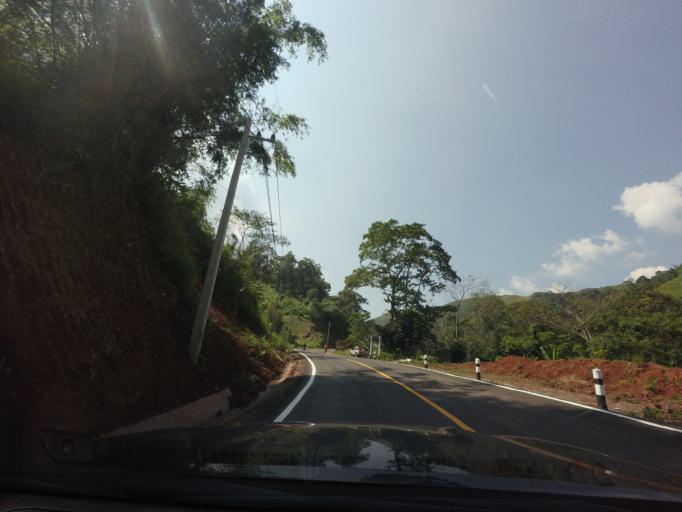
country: TH
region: Nan
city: Bo Kluea
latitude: 19.1952
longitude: 101.1825
